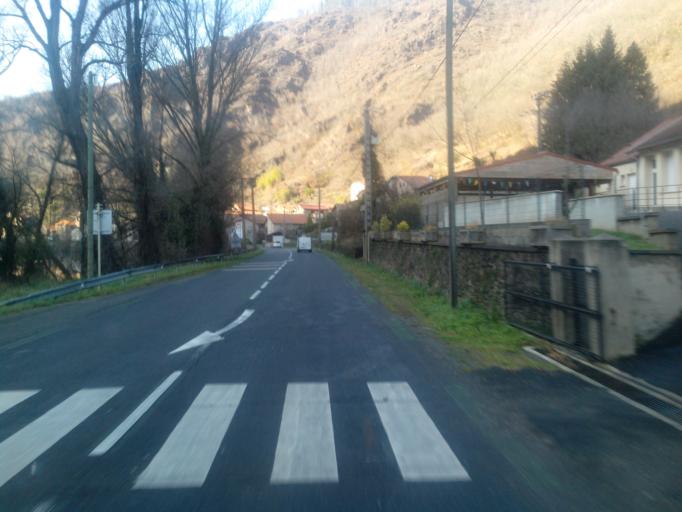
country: FR
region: Midi-Pyrenees
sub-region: Departement de l'Aveyron
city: Viviez
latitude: 44.5818
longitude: 2.1934
